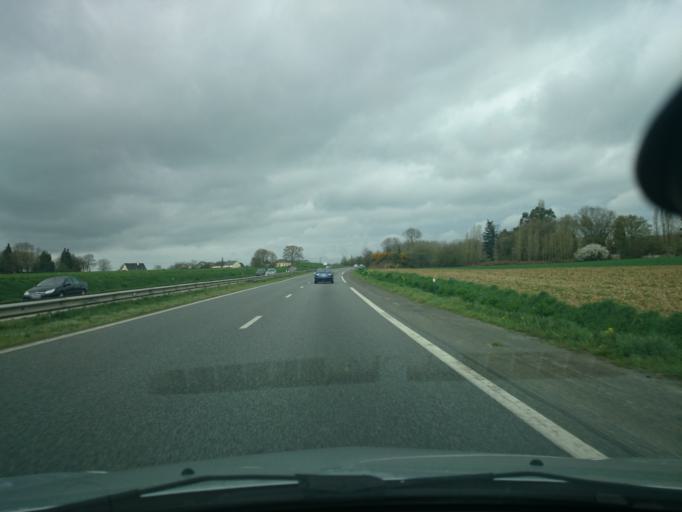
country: FR
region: Brittany
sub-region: Departement d'Ille-et-Vilaine
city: Saint-Gilles
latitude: 48.1606
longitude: -1.8485
